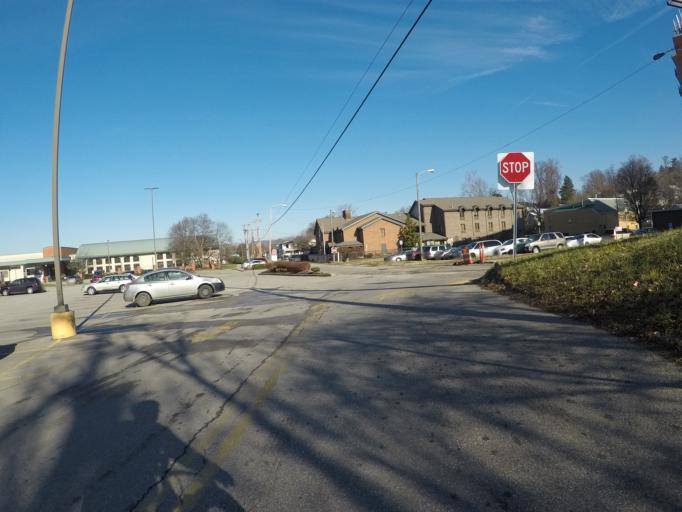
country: US
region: West Virginia
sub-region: Cabell County
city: Huntington
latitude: 38.4087
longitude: -82.4243
